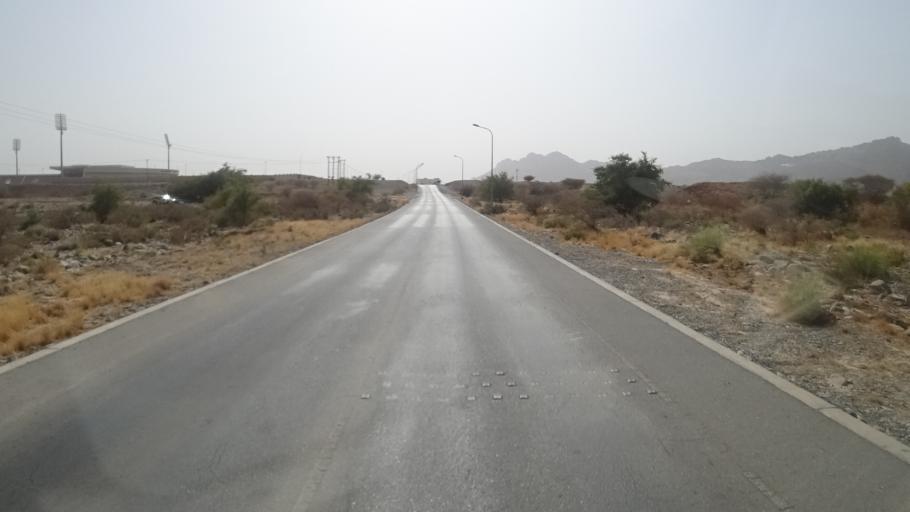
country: OM
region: Muhafazat ad Dakhiliyah
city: Nizwa
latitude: 22.9091
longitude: 57.5917
